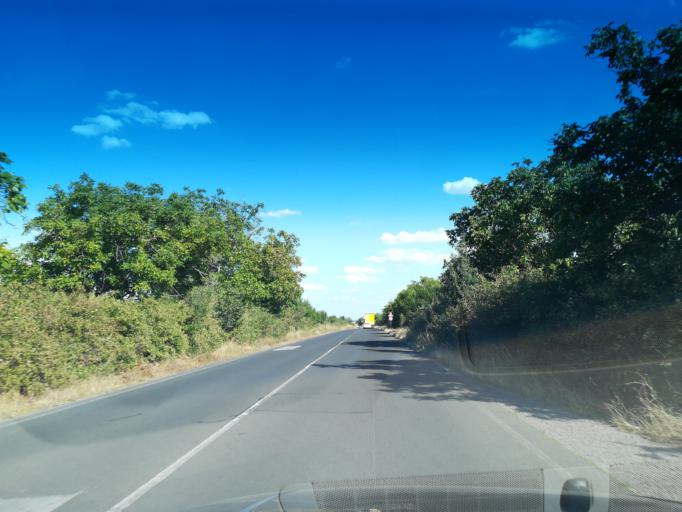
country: BG
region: Stara Zagora
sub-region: Obshtina Chirpan
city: Chirpan
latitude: 42.0599
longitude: 25.2460
